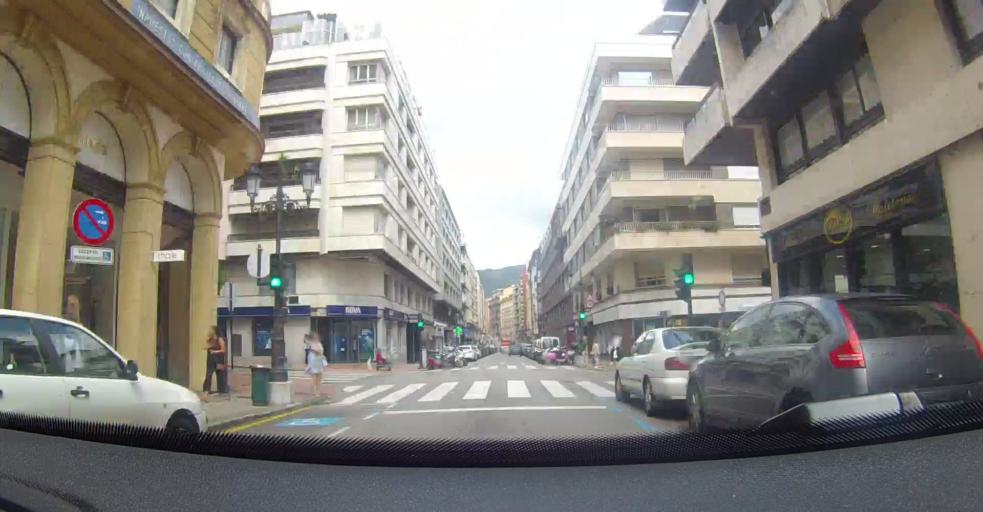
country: ES
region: Asturias
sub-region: Province of Asturias
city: Oviedo
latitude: 43.3635
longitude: -5.8526
